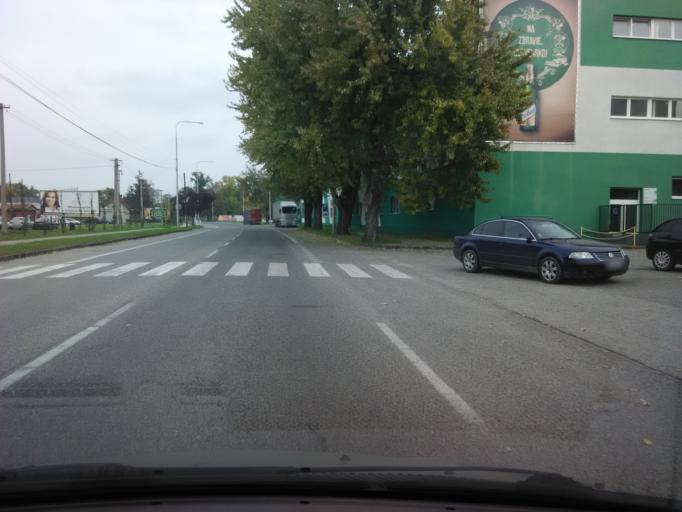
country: SK
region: Nitriansky
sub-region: Okres Komarno
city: Hurbanovo
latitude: 47.8810
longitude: 18.1969
